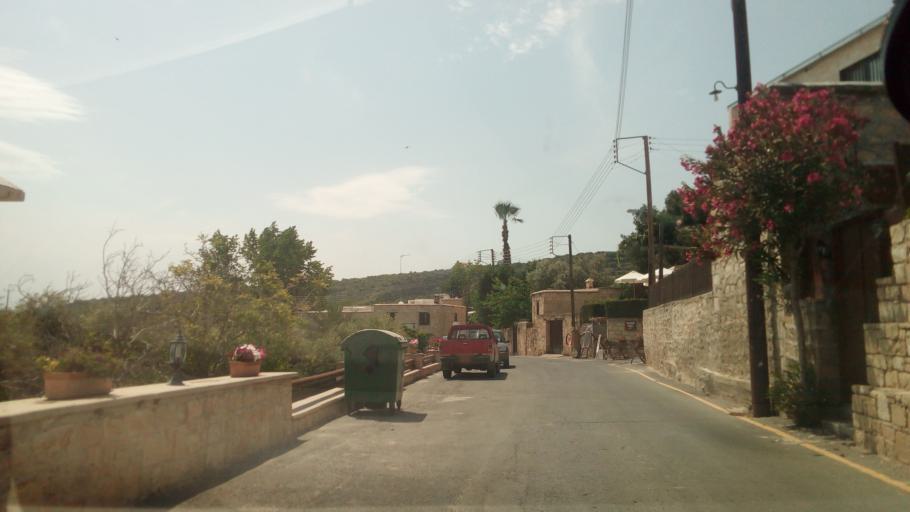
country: CY
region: Pafos
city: Polis
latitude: 34.9533
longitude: 32.4510
